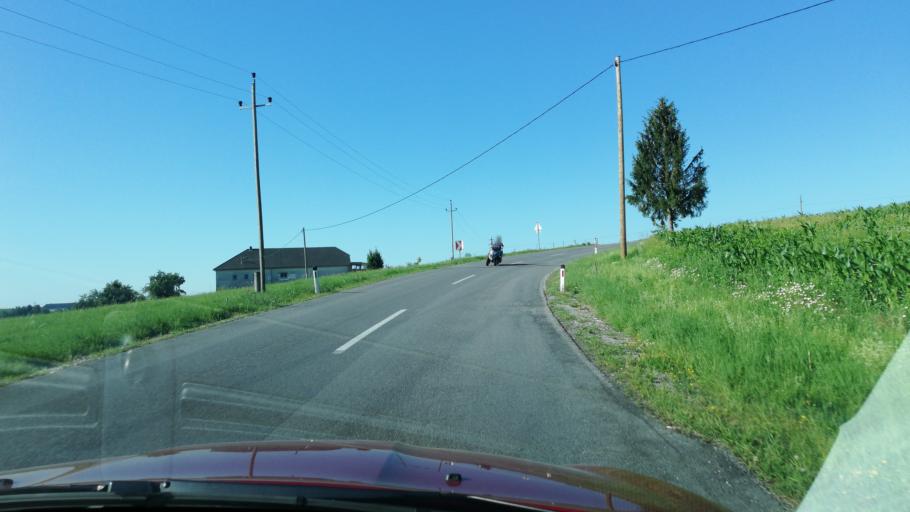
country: AT
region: Upper Austria
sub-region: Politischer Bezirk Urfahr-Umgebung
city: Herzogsdorf
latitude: 48.4642
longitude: 14.0577
